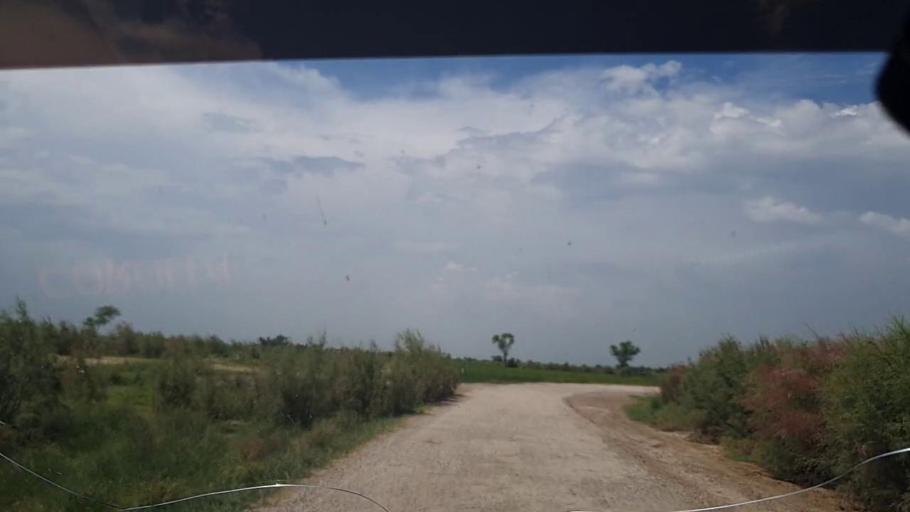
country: PK
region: Sindh
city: Ghauspur
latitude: 28.1477
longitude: 68.9808
